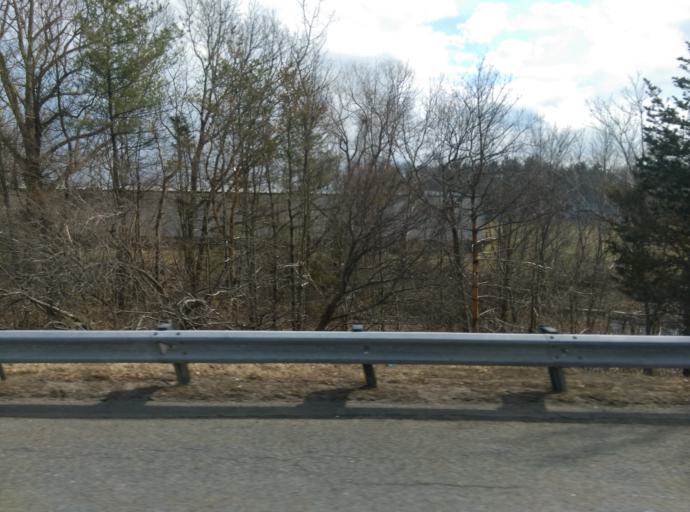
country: US
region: Massachusetts
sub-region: Essex County
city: Merrimac
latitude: 42.8346
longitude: -70.9633
